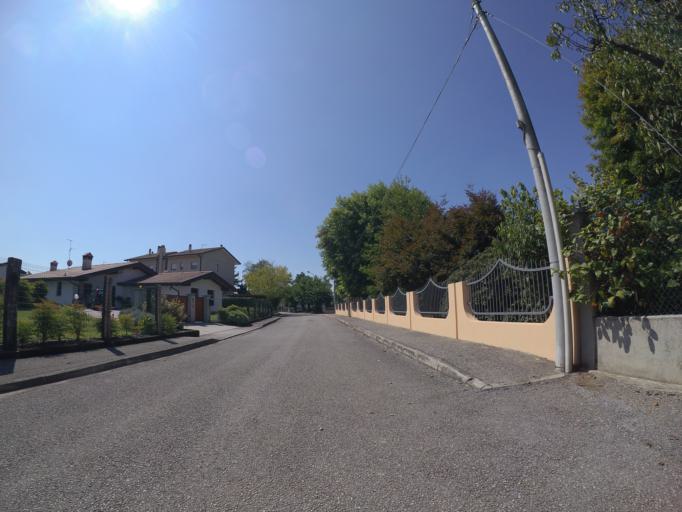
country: IT
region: Friuli Venezia Giulia
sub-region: Provincia di Udine
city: Talmassons
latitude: 45.9381
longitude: 13.0919
